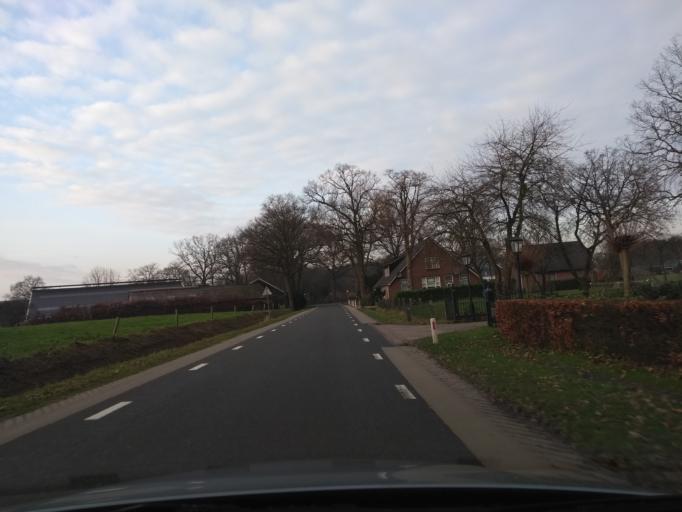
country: NL
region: Overijssel
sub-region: Gemeente Almelo
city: Almelo
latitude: 52.3206
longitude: 6.6933
